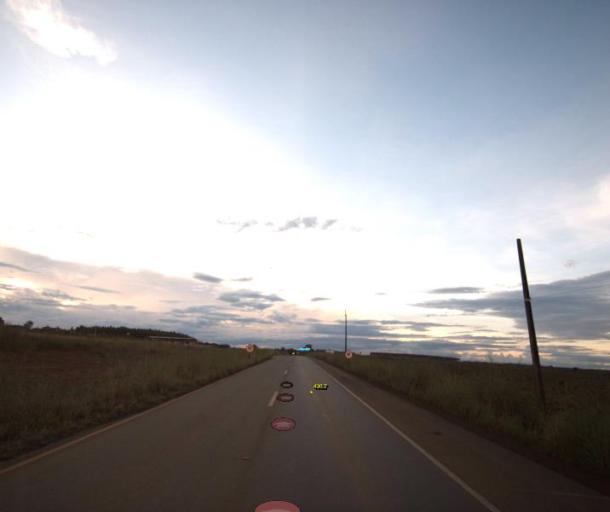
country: BR
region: Goias
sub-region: Anapolis
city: Anapolis
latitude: -16.2503
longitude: -48.9955
